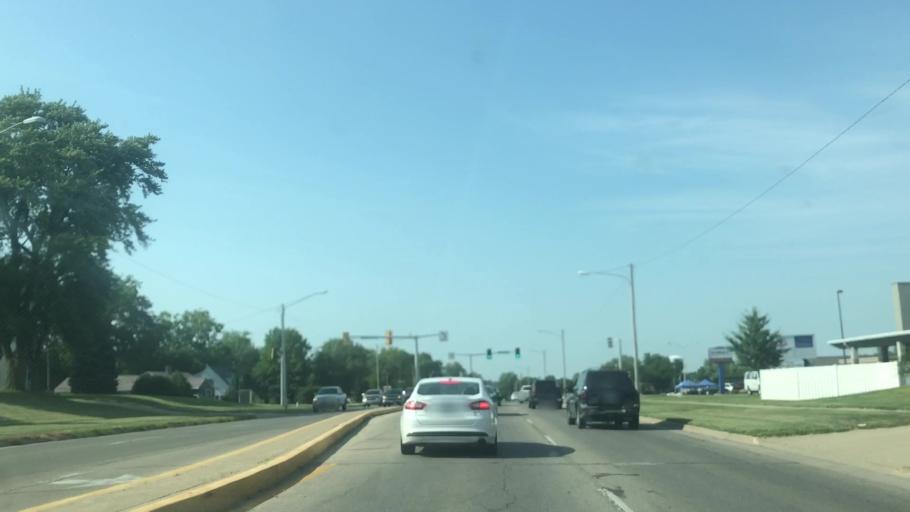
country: US
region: Iowa
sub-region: Marshall County
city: Marshalltown
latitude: 42.0245
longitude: -92.9125
